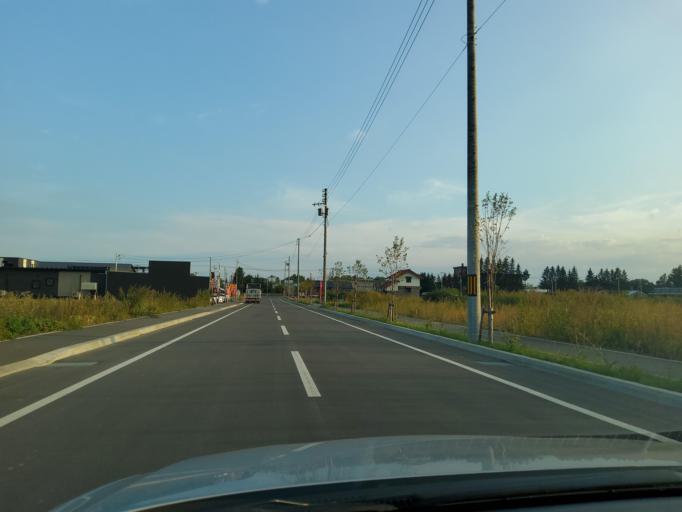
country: JP
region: Hokkaido
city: Obihiro
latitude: 42.9355
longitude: 143.1534
